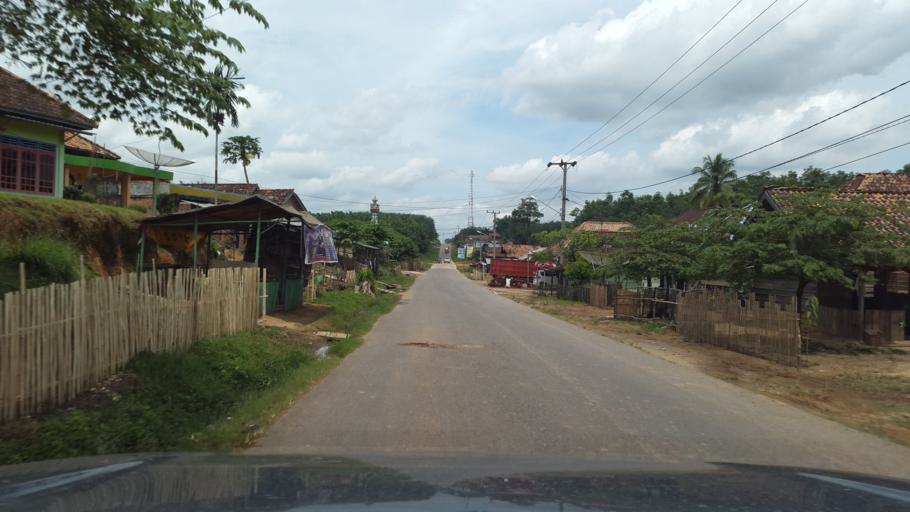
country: ID
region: South Sumatra
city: Gunungmegang Dalam
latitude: -3.3361
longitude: 103.9101
